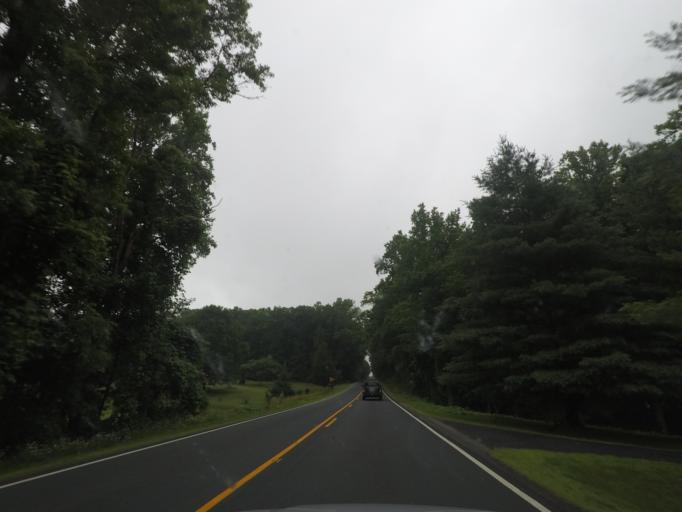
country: US
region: Virginia
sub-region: Charlotte County
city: Charlotte Court House
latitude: 37.0778
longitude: -78.4765
